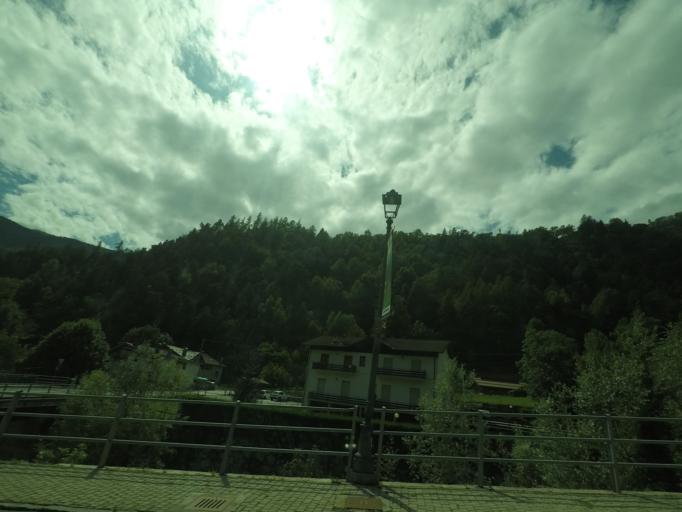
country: IT
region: Aosta Valley
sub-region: Valle d'Aosta
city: Antey-Saint-Andre
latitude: 45.8018
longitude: 7.5899
